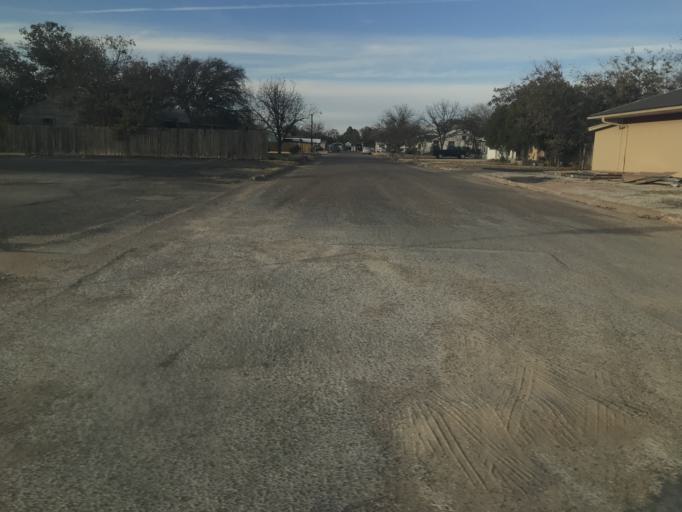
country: US
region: Texas
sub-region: Taylor County
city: Abilene
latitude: 32.4323
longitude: -99.7560
